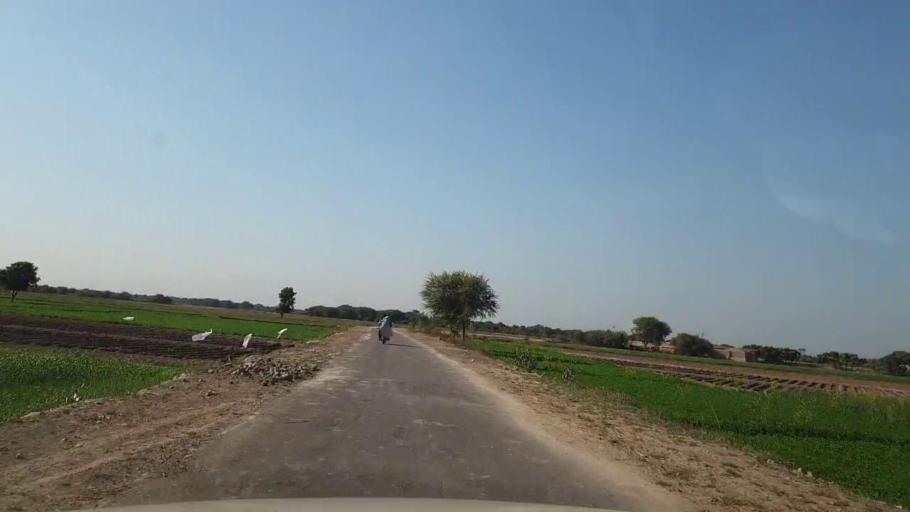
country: PK
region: Sindh
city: Tando Allahyar
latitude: 25.4855
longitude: 68.6576
